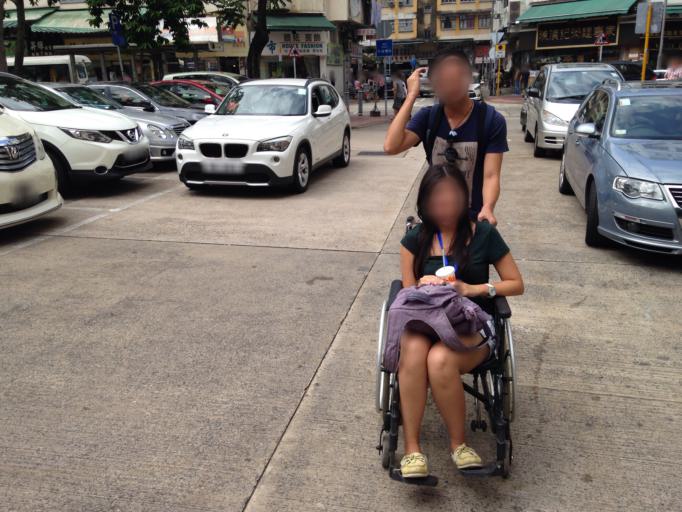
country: HK
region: Tai Po
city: Tai Po
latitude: 22.4468
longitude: 114.1683
